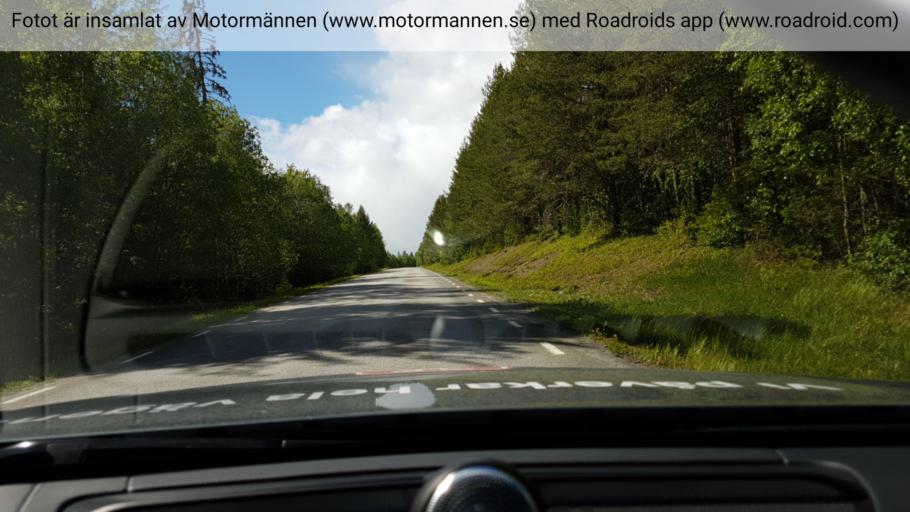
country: SE
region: Jaemtland
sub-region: Krokoms Kommun
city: Krokom
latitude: 63.2724
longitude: 14.3641
